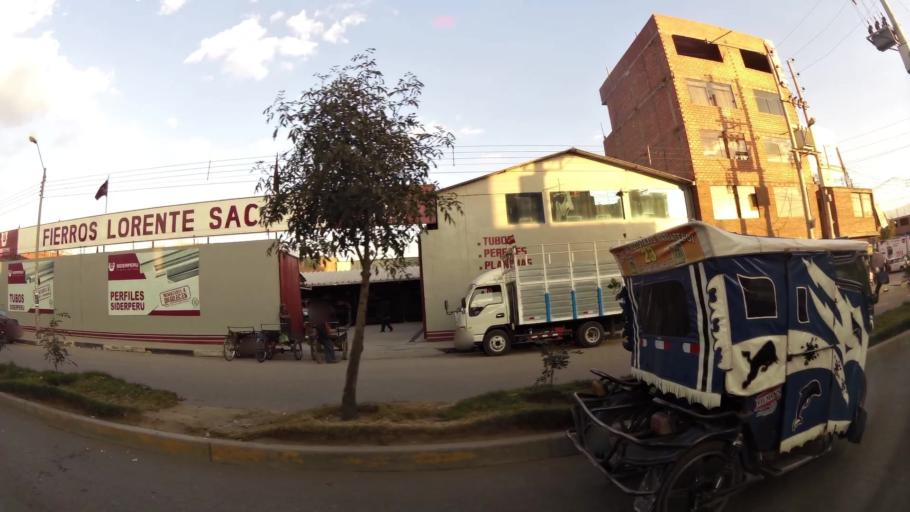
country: PE
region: Junin
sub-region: Provincia de Huancayo
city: El Tambo
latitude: -12.0564
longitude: -75.2229
